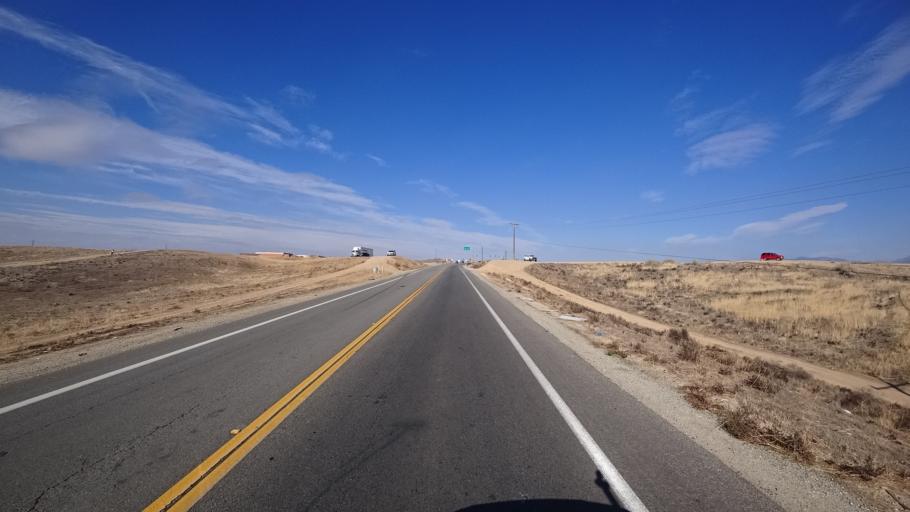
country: US
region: California
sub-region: Kern County
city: Bakersfield
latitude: 35.3902
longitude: -118.9143
